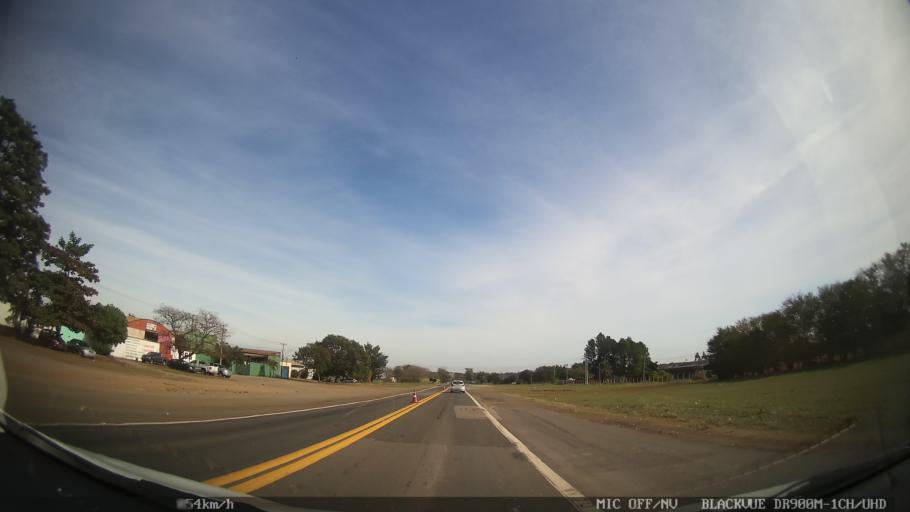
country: BR
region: Sao Paulo
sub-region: Rio Das Pedras
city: Rio das Pedras
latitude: -22.7943
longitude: -47.6177
